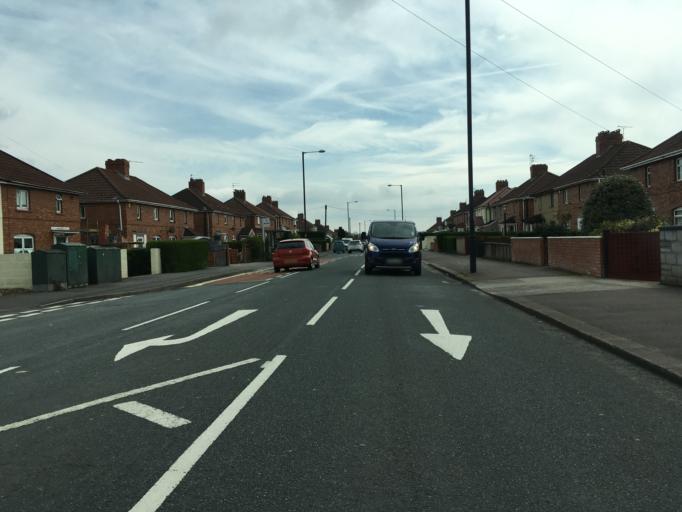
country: GB
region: England
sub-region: South Gloucestershire
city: Almondsbury
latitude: 51.5089
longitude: -2.5981
